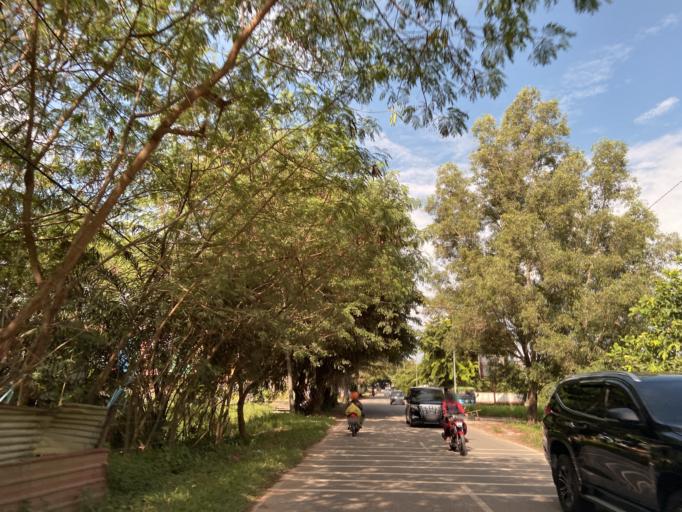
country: SG
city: Singapore
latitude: 1.1121
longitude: 104.0364
